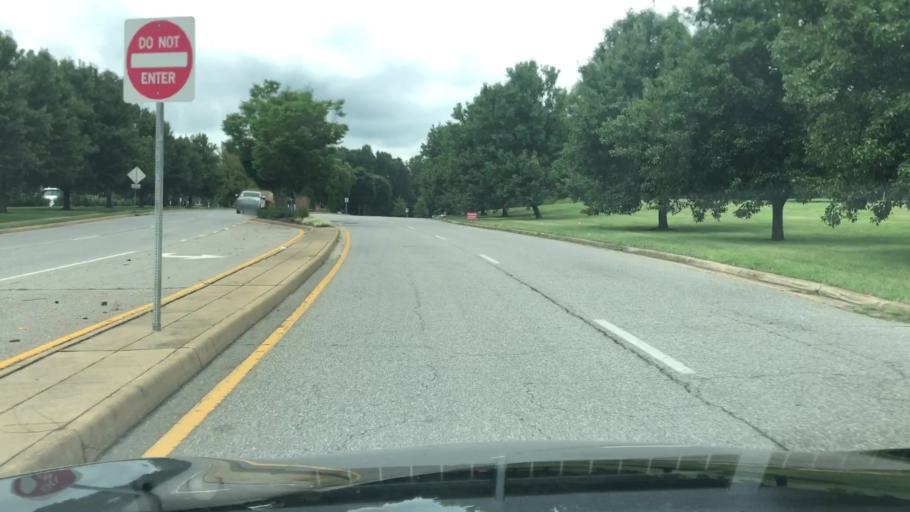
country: US
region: Virginia
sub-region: Stafford County
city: Falmouth
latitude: 38.3703
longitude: -77.5308
